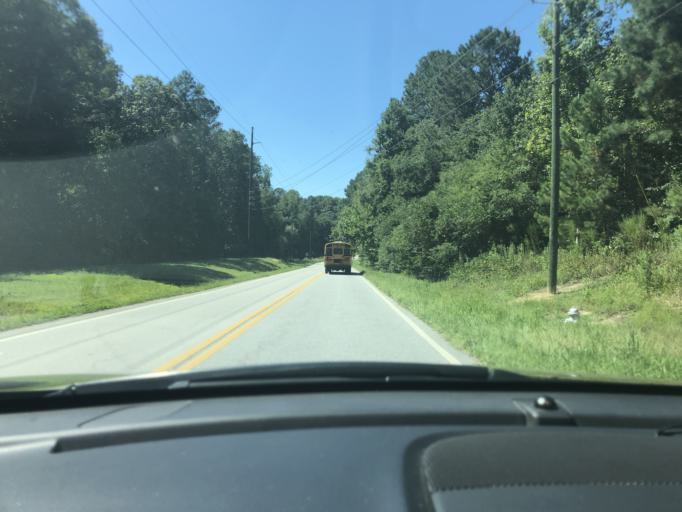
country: US
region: Georgia
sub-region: Gwinnett County
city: Grayson
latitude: 33.9182
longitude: -83.9402
